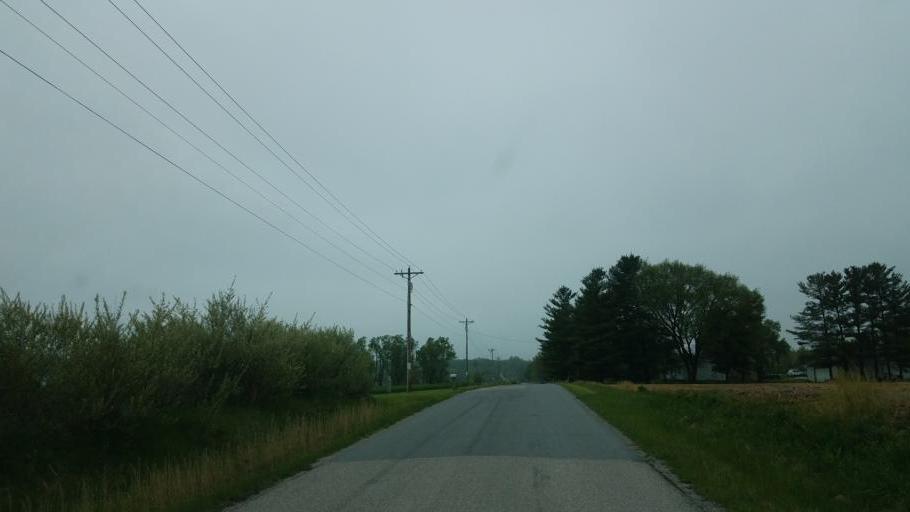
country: US
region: Ohio
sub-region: Knox County
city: Fredericktown
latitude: 40.4704
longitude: -82.6474
